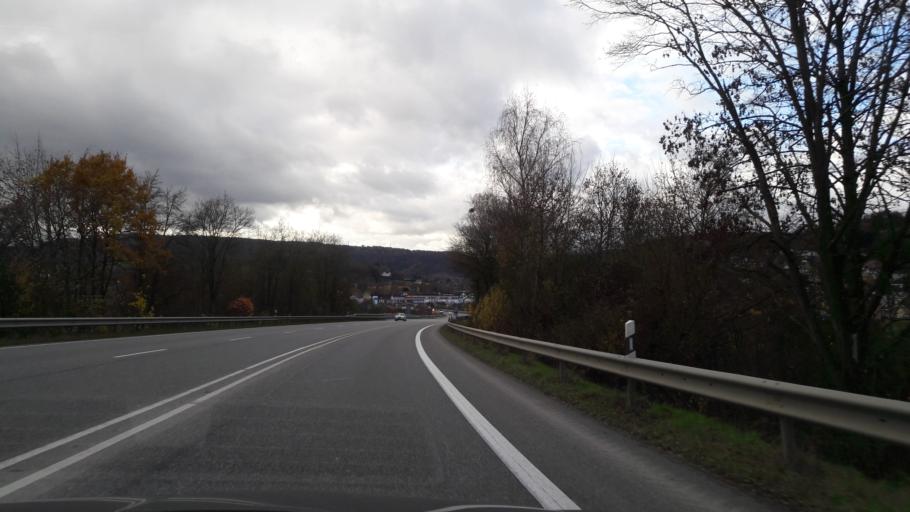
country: DE
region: Rheinland-Pfalz
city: Echternacherbruck
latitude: 49.8177
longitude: 6.4416
